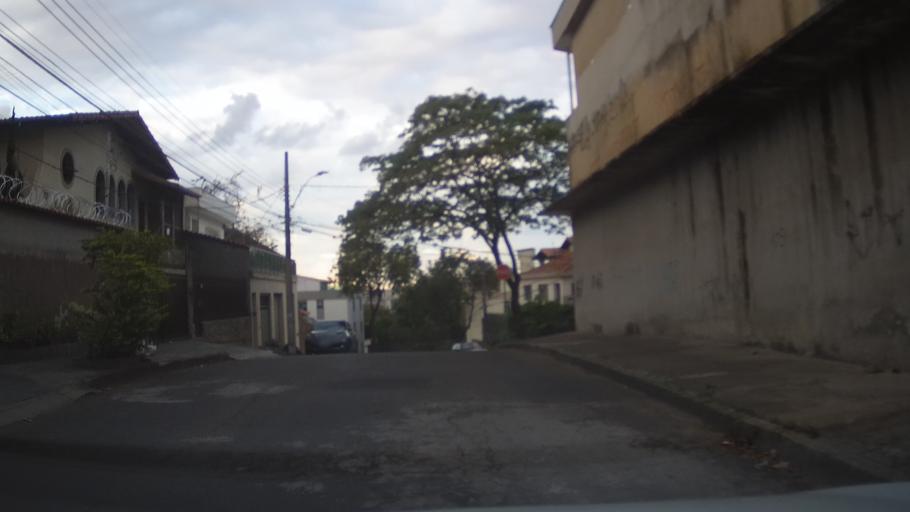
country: BR
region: Minas Gerais
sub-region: Belo Horizonte
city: Belo Horizonte
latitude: -19.8952
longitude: -43.9347
